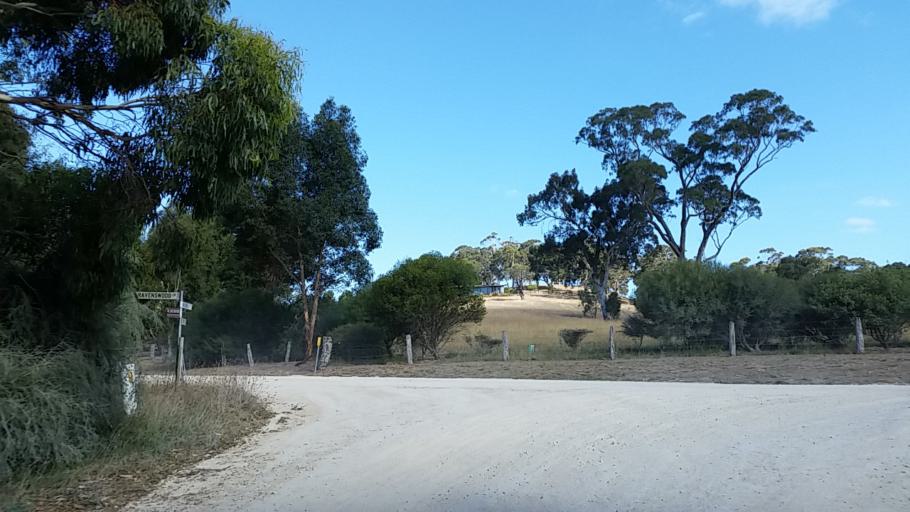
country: AU
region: South Australia
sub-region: Adelaide Hills
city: Balhannah
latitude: -35.0155
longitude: 138.8399
